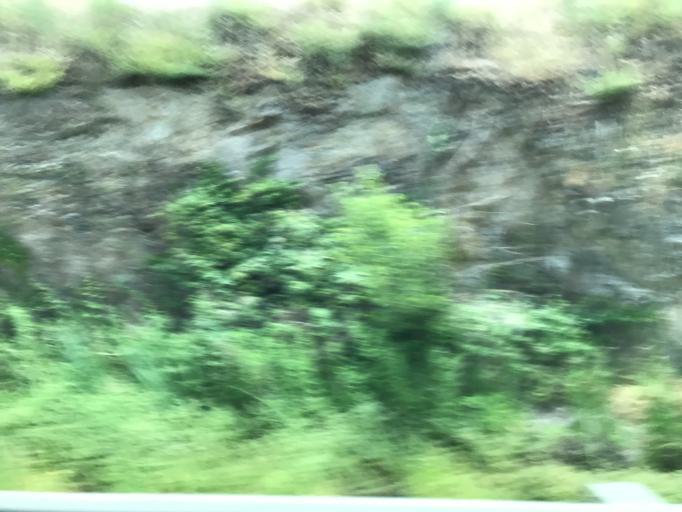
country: ES
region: Madrid
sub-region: Provincia de Madrid
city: Buitrago del Lozoya
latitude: 40.9987
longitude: -3.6402
